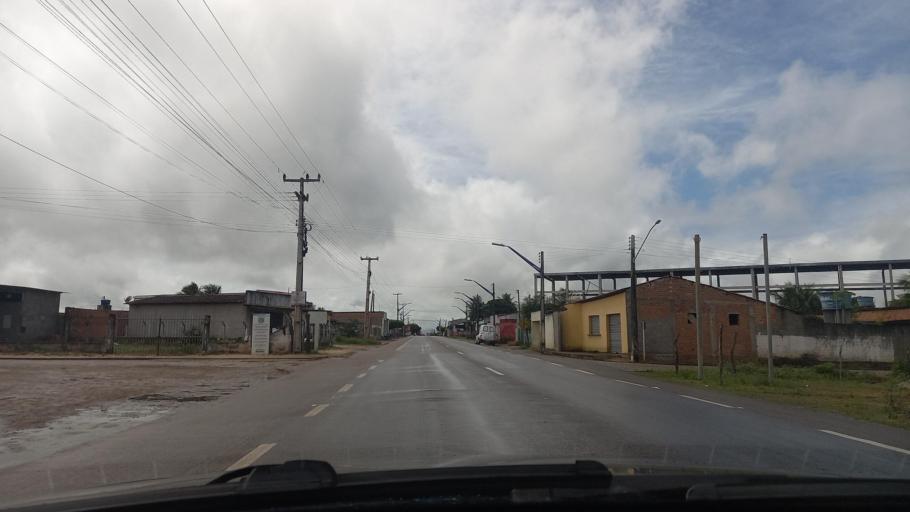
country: BR
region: Alagoas
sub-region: Limoeiro De Anadia
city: Limoeiro de Anadia
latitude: -9.7585
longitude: -36.5594
